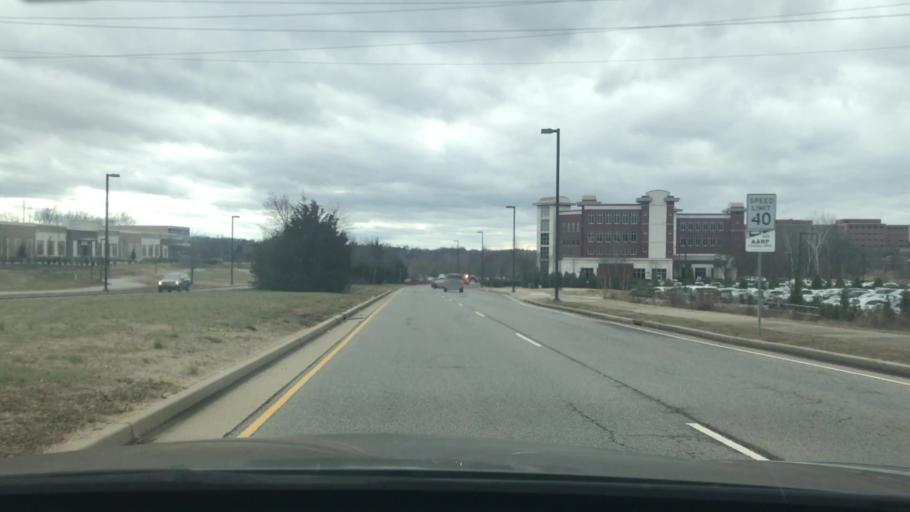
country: US
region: Tennessee
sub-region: Williamson County
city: Franklin
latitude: 35.9218
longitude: -86.8167
